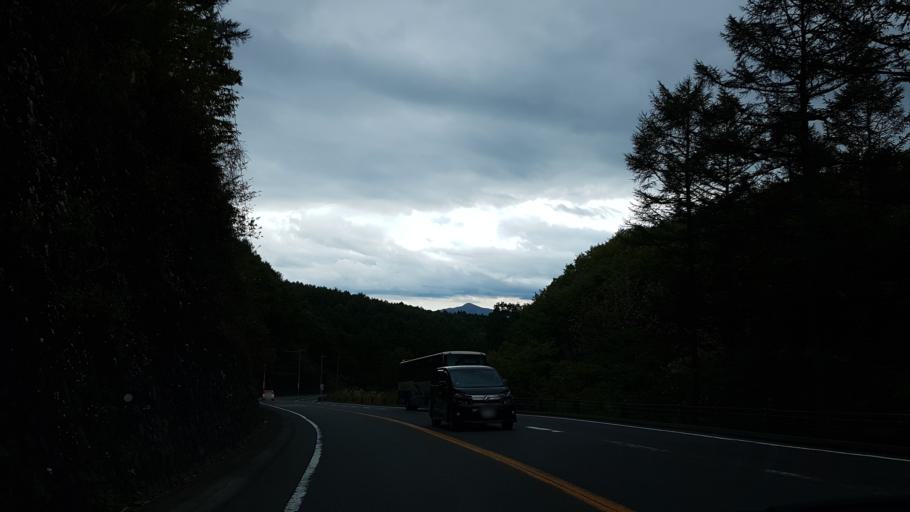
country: JP
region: Gunma
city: Nakanojomachi
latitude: 36.6023
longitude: 138.5851
